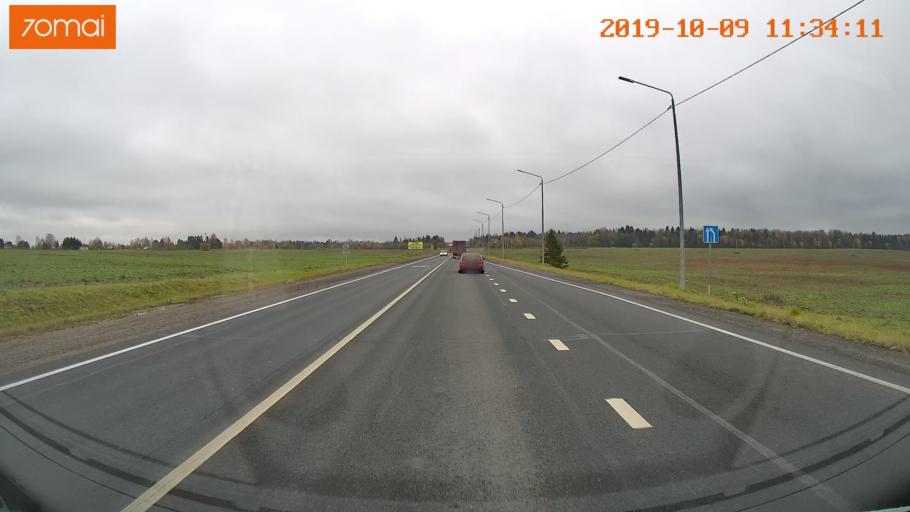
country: RU
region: Vologda
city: Gryazovets
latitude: 59.0187
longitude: 40.1166
